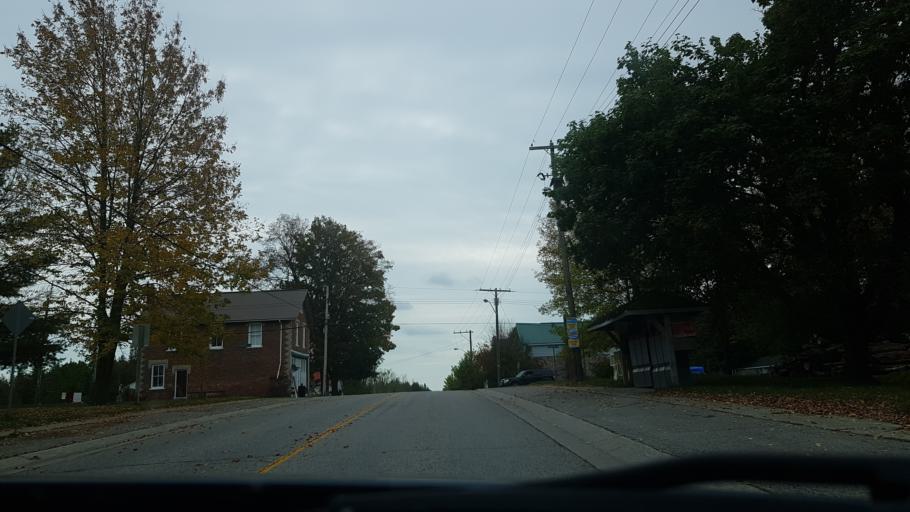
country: CA
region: Ontario
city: Omemee
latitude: 44.5955
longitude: -78.9393
